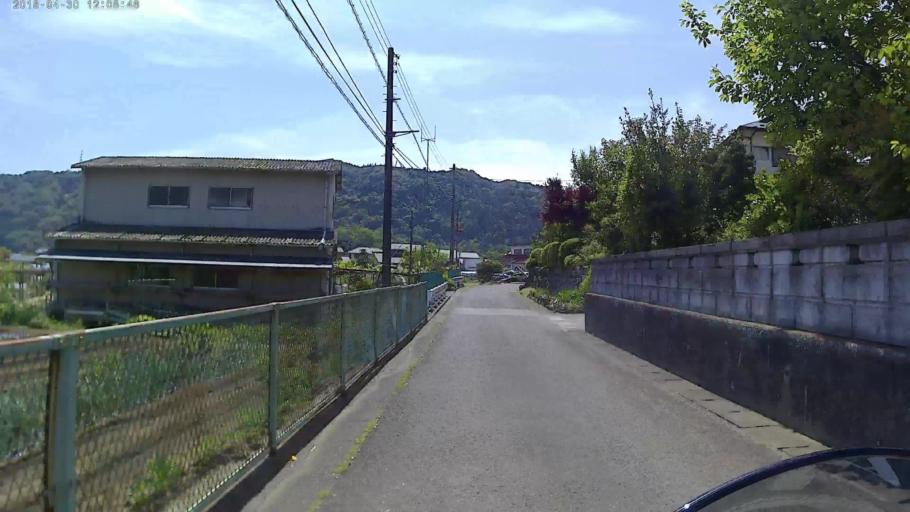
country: JP
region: Kanagawa
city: Zama
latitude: 35.5301
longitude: 139.3086
